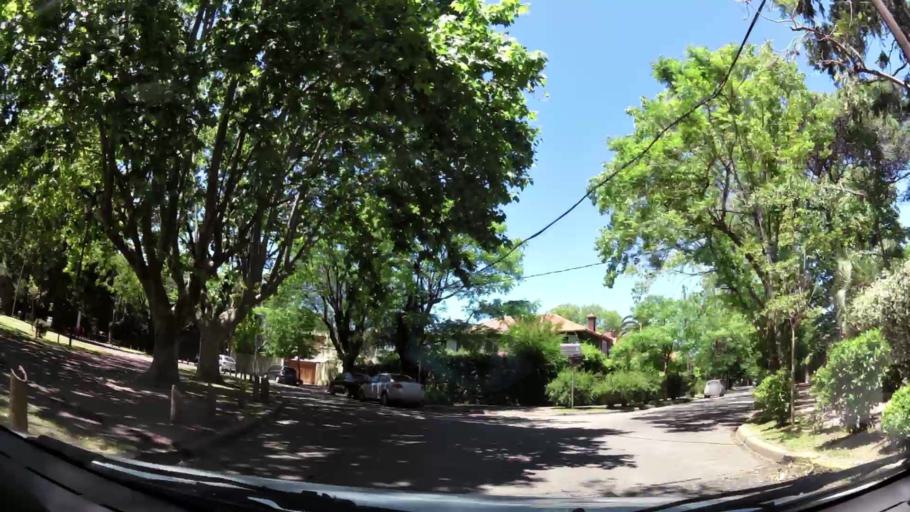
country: AR
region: Buenos Aires
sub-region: Partido de San Isidro
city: San Isidro
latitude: -34.4749
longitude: -58.5067
